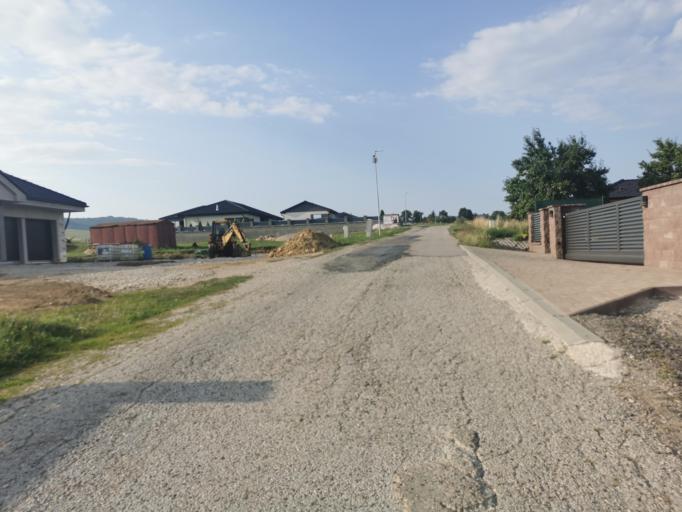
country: SK
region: Trenciansky
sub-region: Okres Myjava
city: Myjava
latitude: 48.7821
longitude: 17.5659
